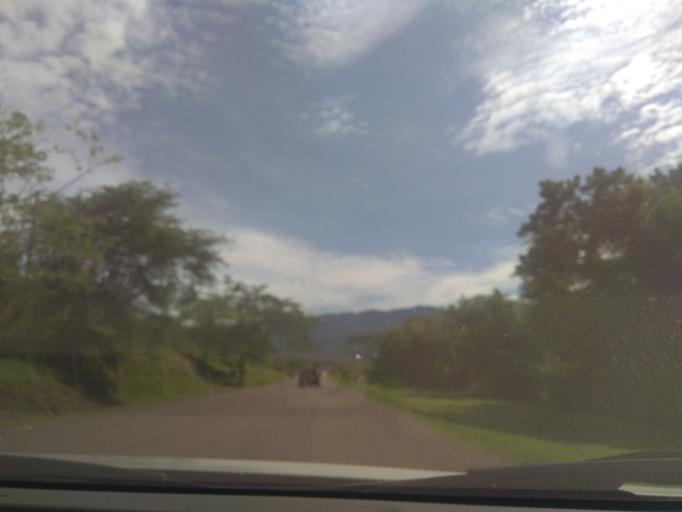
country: HN
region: Intibuca
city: Jesus de Otoro
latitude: 14.4766
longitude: -87.9930
